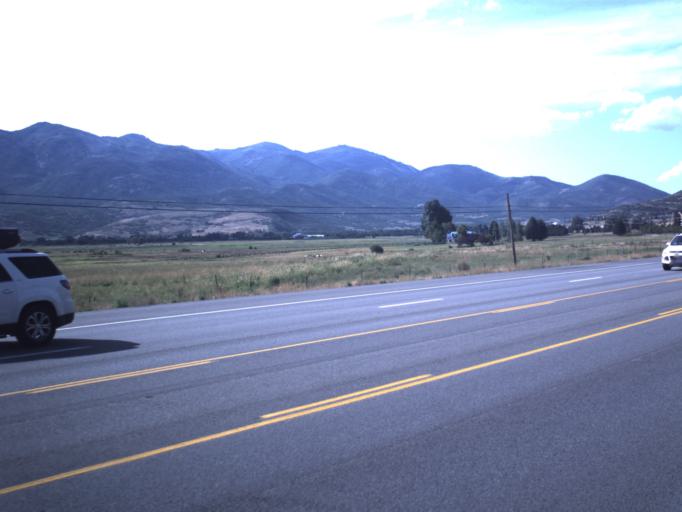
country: US
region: Utah
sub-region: Wasatch County
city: Heber
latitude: 40.5313
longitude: -111.4093
